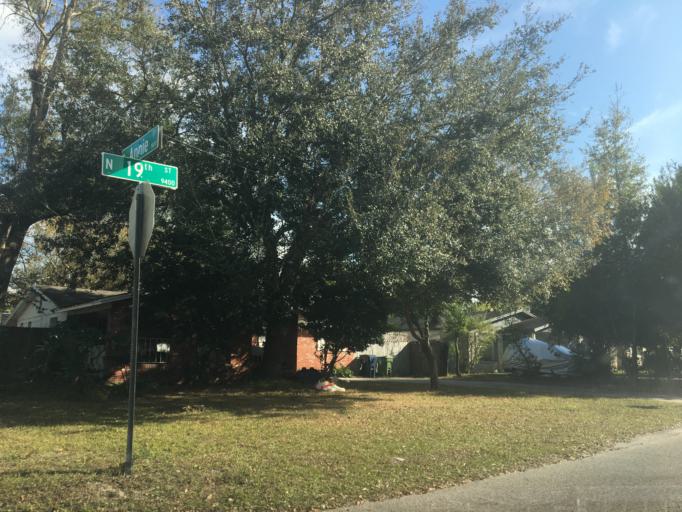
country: US
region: Florida
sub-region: Hillsborough County
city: University
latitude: 28.0362
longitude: -82.4376
